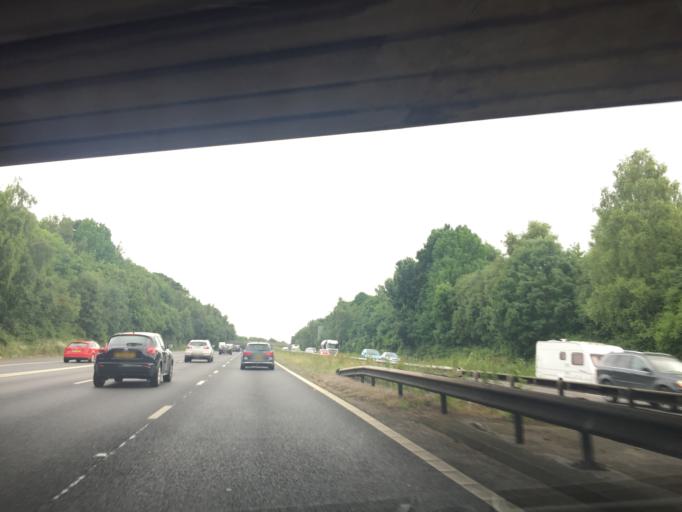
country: GB
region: England
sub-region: Hampshire
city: Chandlers Ford
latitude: 50.9974
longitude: -1.3574
